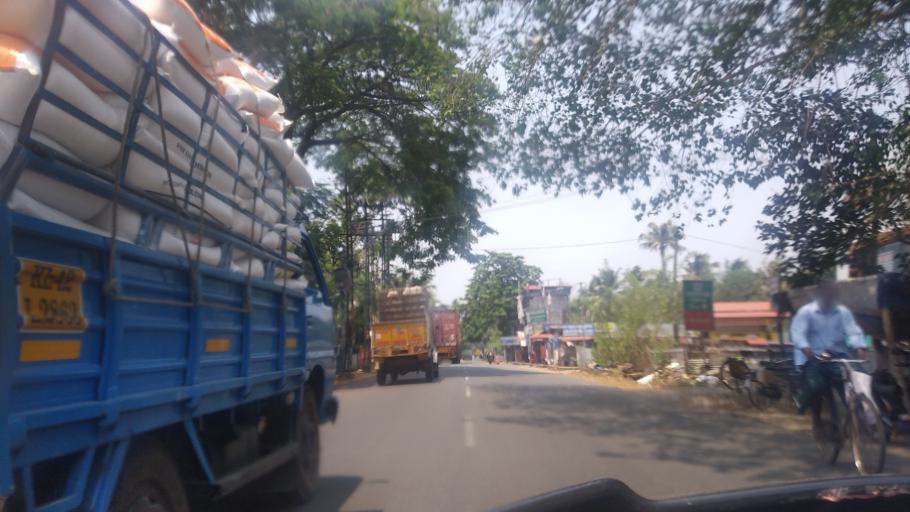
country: IN
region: Kerala
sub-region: Thrissur District
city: Kodungallur
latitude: 10.2377
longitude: 76.1933
